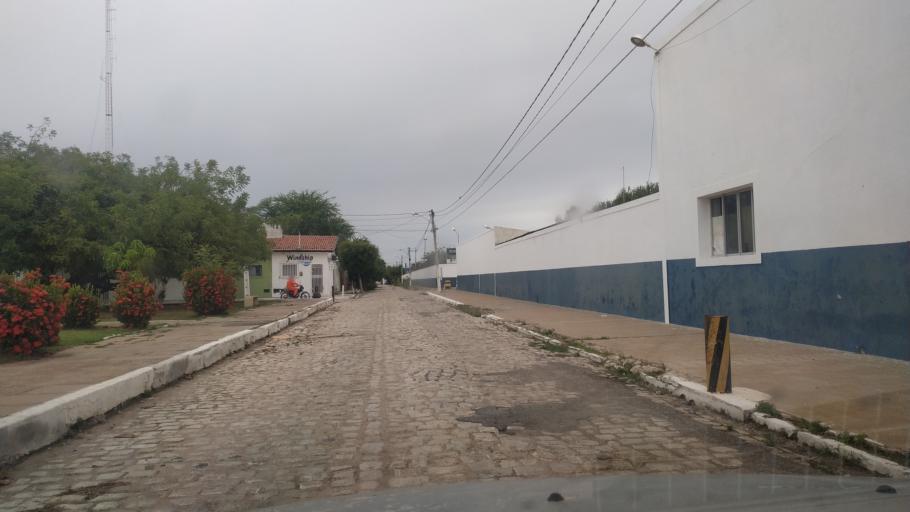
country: BR
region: Rio Grande do Norte
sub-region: Areia Branca
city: Areia Branca
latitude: -4.9583
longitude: -37.1377
